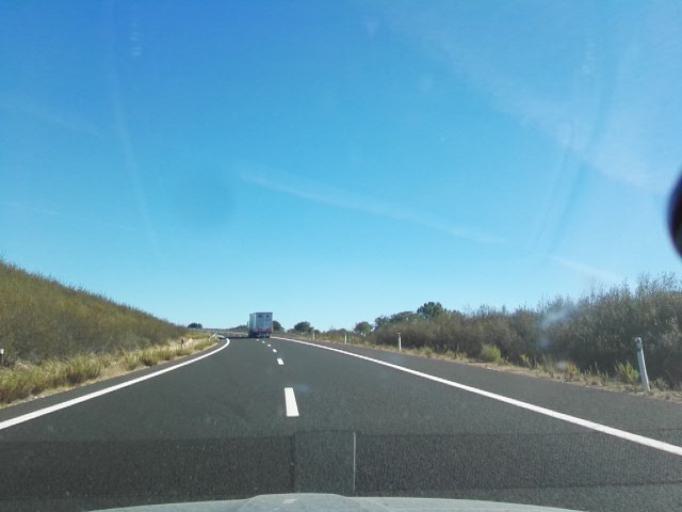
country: PT
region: Santarem
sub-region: Benavente
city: Poceirao
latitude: 38.8996
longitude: -8.7841
